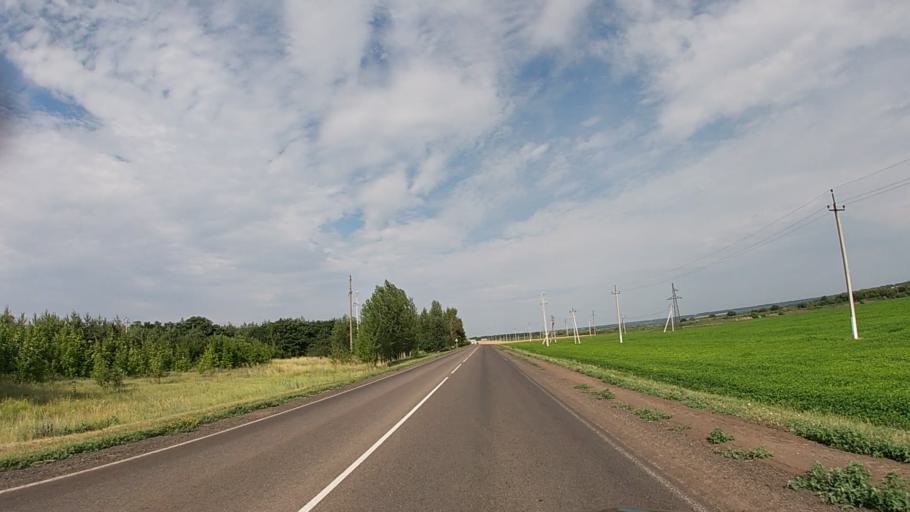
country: RU
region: Belgorod
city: Krasnaya Yaruga
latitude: 50.7977
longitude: 35.6255
